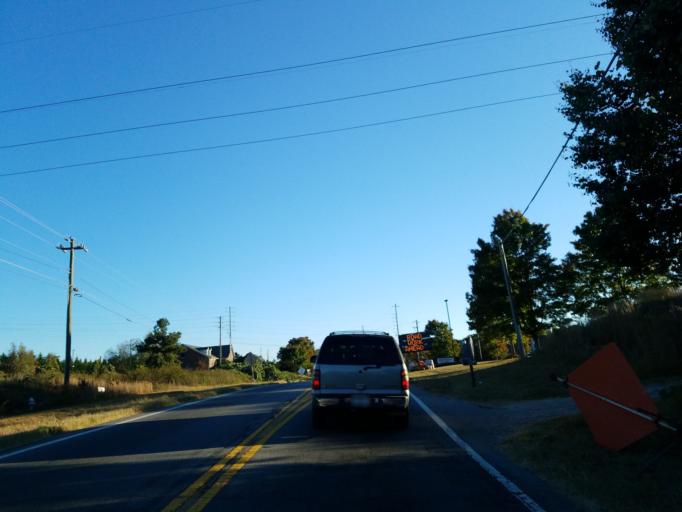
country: US
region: Georgia
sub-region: Dawson County
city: Dawsonville
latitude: 34.3710
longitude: -84.0420
